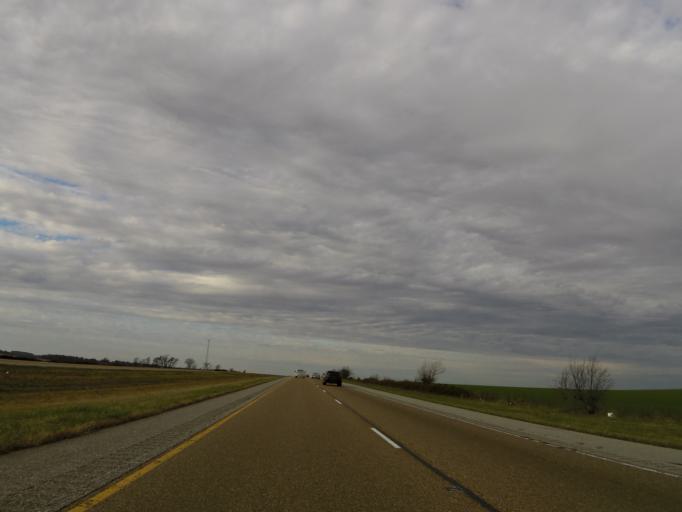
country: US
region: Illinois
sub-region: Washington County
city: Nashville
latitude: 38.3903
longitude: -89.2412
